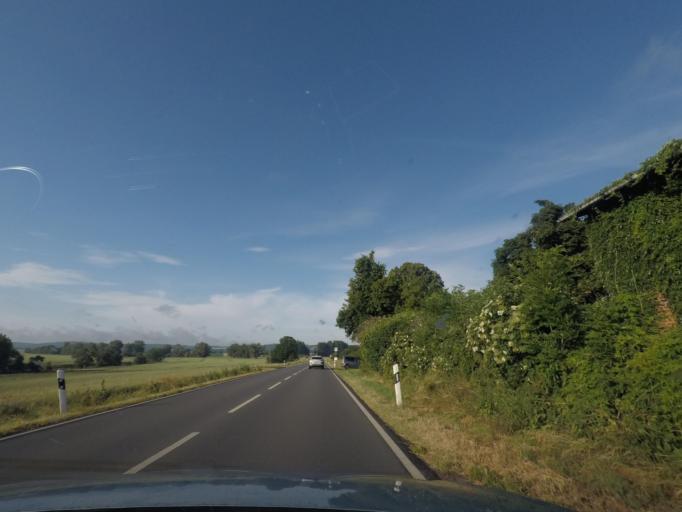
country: DE
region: Saxony-Anhalt
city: Huy-Neinstedt
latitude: 52.0082
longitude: 10.8967
